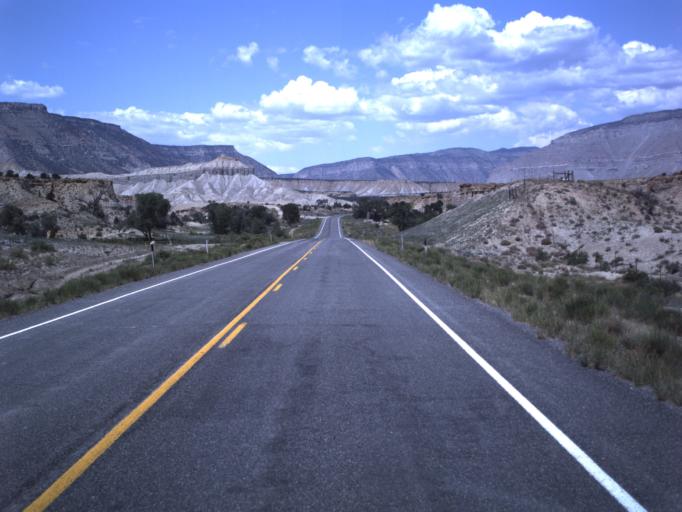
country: US
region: Utah
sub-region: Emery County
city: Orangeville
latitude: 39.2328
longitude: -111.0793
